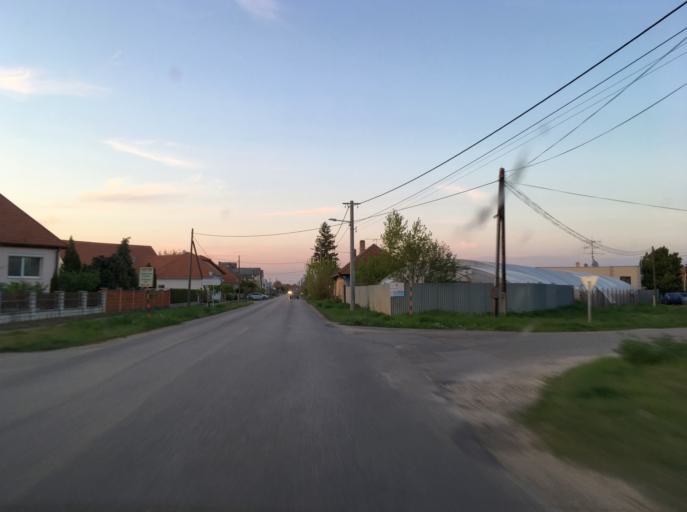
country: SK
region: Nitriansky
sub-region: Okres Nove Zamky
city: Nove Zamky
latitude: 47.9291
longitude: 18.1219
